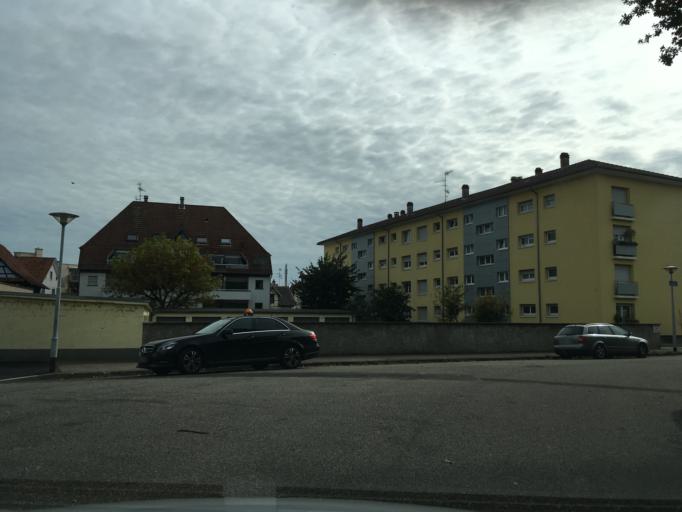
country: FR
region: Alsace
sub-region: Departement du Bas-Rhin
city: Bischheim
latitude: 48.6080
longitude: 7.7773
